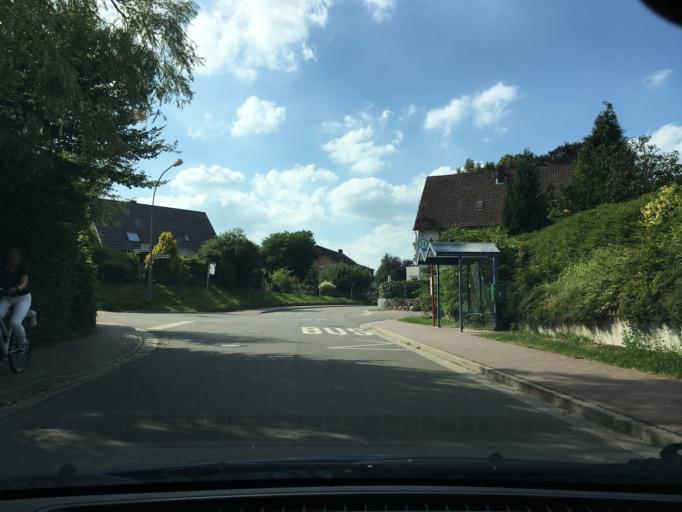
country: DE
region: Lower Saxony
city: Bendestorf
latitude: 53.3656
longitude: 9.9425
